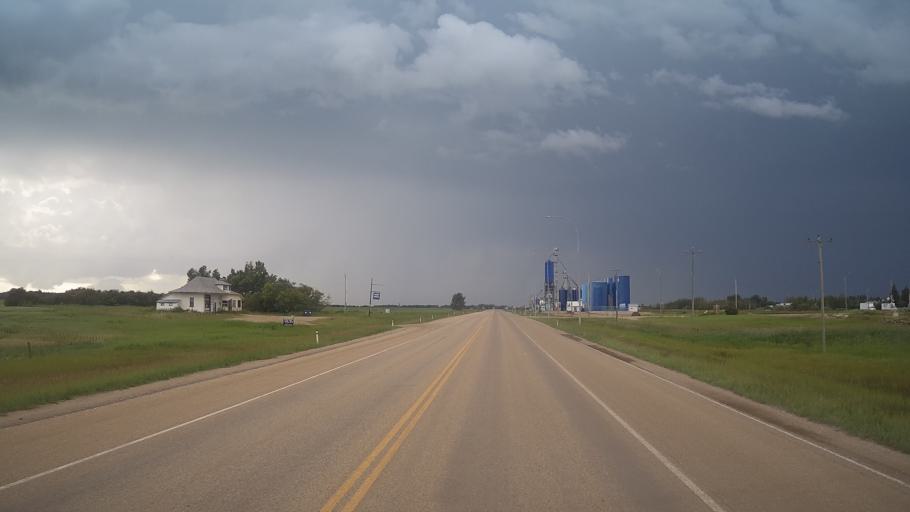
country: CA
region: Alberta
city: Tofield
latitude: 53.2866
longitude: -112.4292
